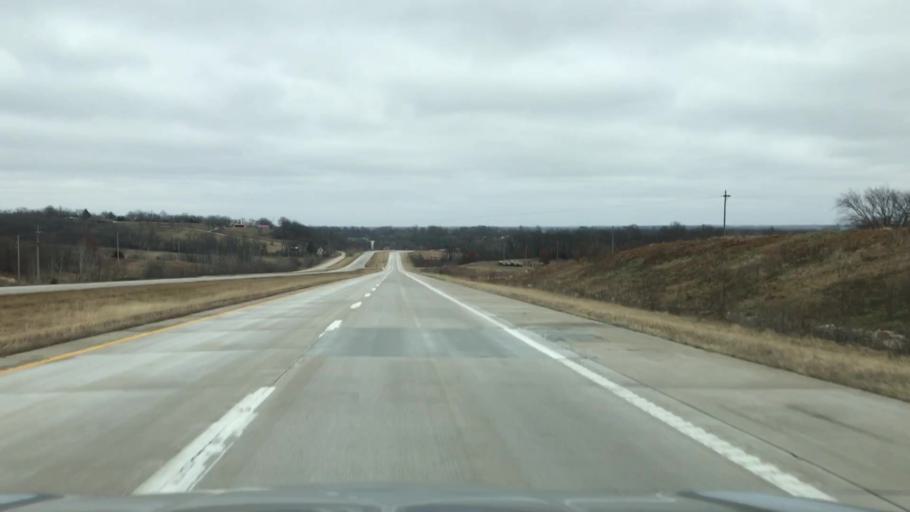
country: US
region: Missouri
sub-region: Livingston County
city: Chillicothe
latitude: 39.7396
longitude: -93.6543
